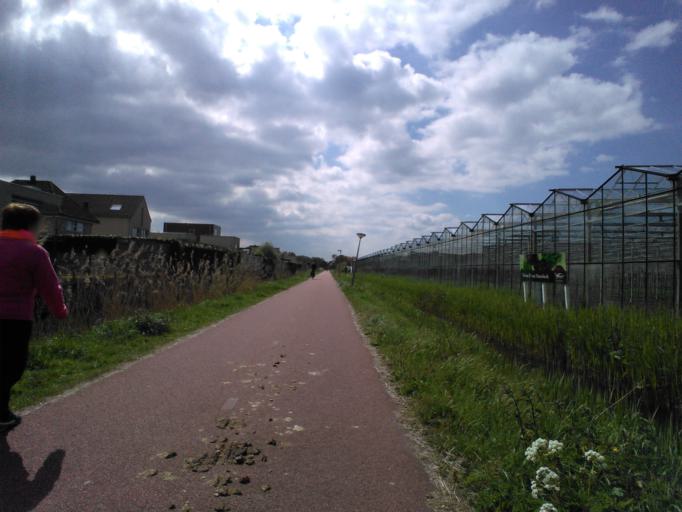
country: NL
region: South Holland
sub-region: Gemeente Rotterdam
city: Hoek van Holland
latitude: 51.9937
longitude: 4.1335
